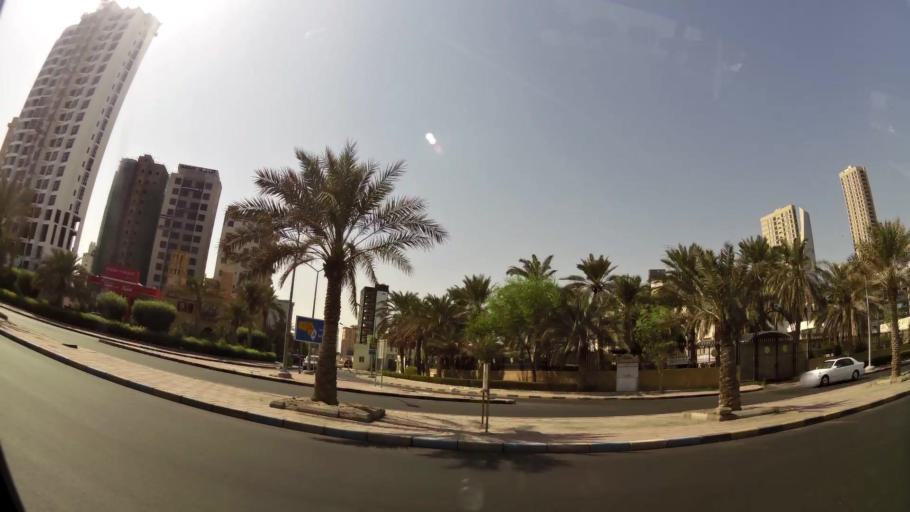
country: KW
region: Al Asimah
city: Ad Dasmah
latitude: 29.3752
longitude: 48.0049
